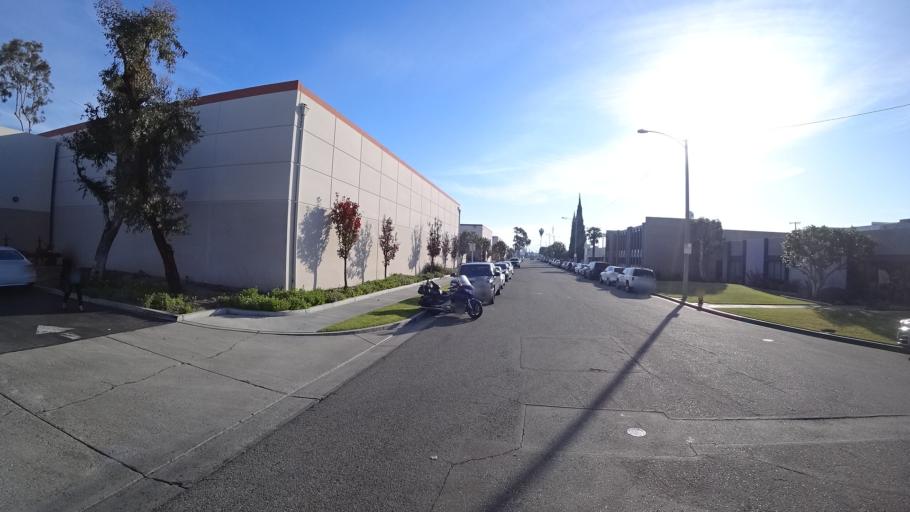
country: US
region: California
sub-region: Orange County
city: Fullerton
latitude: 33.8559
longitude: -117.9100
